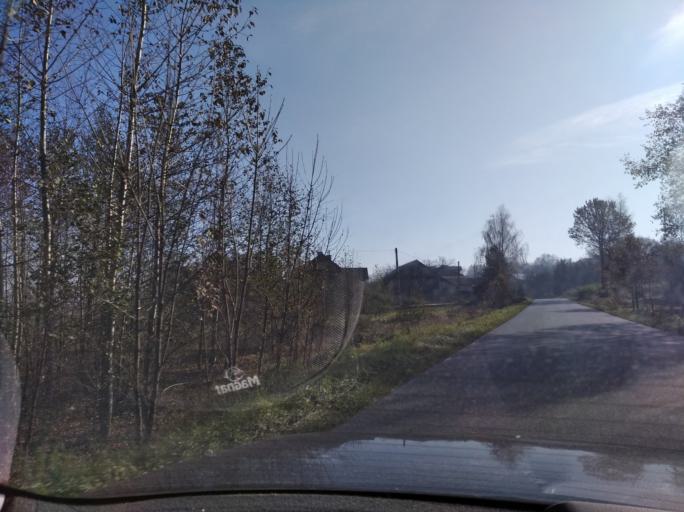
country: PL
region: Subcarpathian Voivodeship
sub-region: Powiat ropczycko-sedziszowski
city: Wielopole Skrzynskie
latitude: 49.9473
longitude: 21.6006
